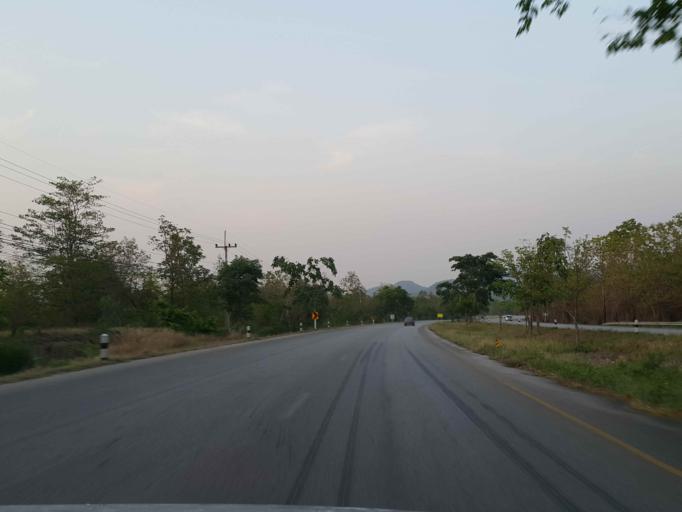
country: TH
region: Lampang
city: Soem Ngam
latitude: 18.0505
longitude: 99.3853
